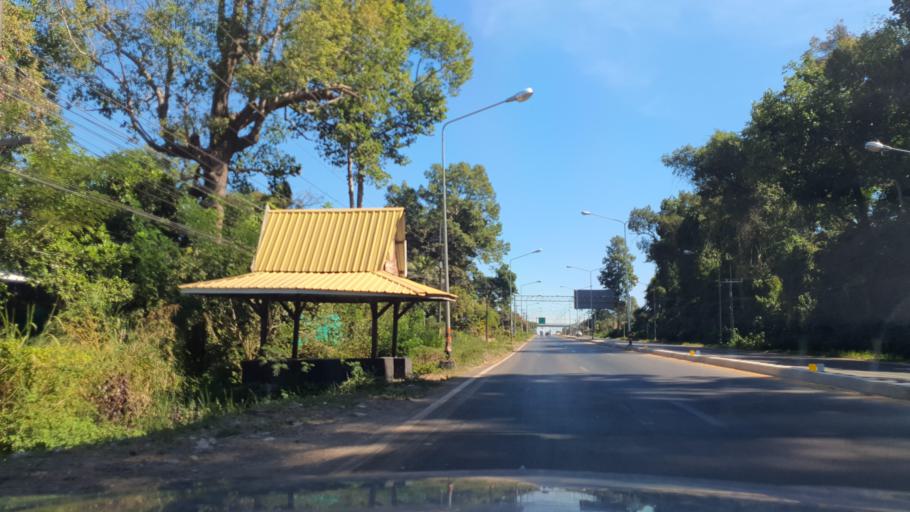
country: TH
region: Sakon Nakhon
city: Sakon Nakhon
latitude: 17.0853
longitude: 104.1866
